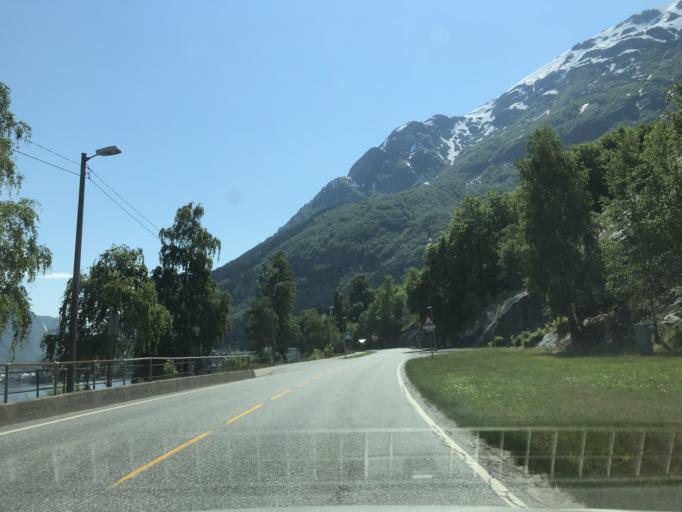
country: NO
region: Hordaland
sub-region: Odda
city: Odda
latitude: 60.0852
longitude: 6.5309
